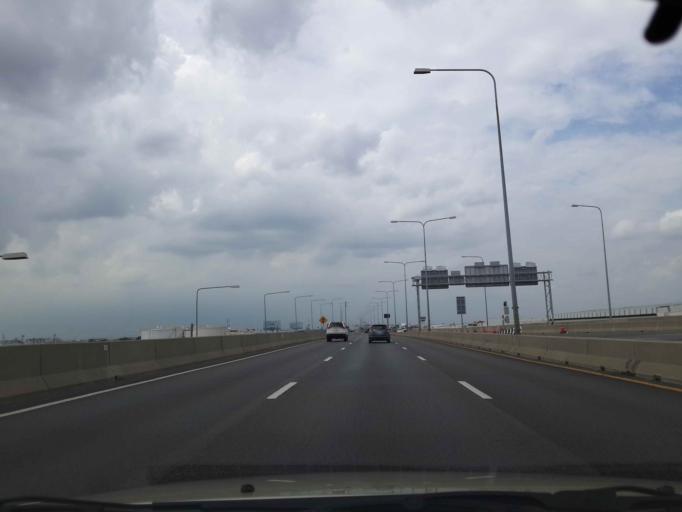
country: TH
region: Bangkok
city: Don Mueang
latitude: 13.8995
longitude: 100.5901
